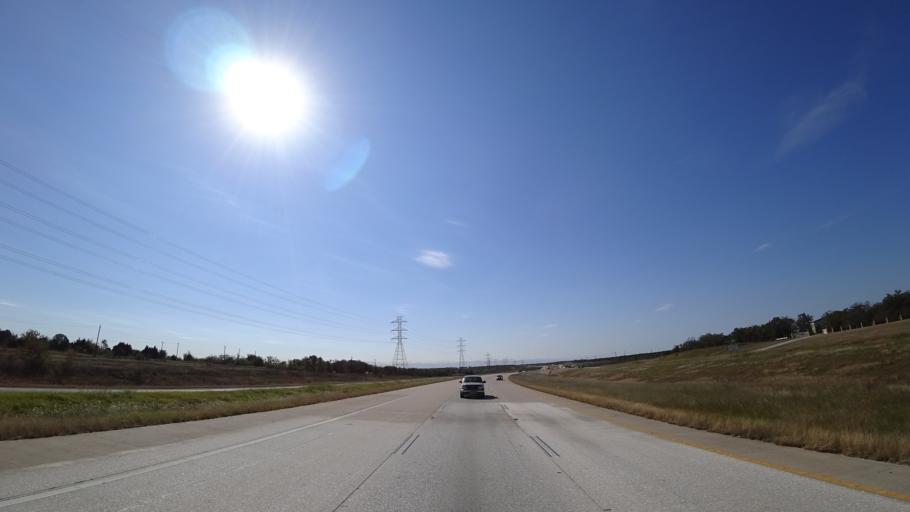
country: US
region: Texas
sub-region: Travis County
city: Hornsby Bend
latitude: 30.2836
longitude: -97.5786
